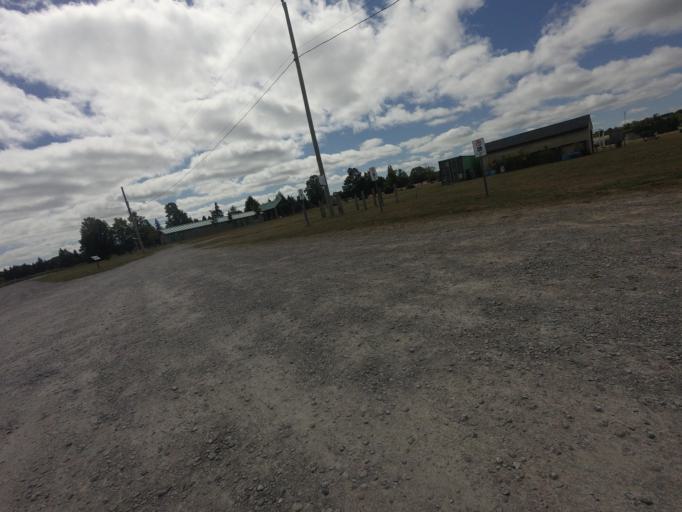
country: CA
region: Ontario
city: Uxbridge
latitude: 44.1270
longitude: -79.1235
